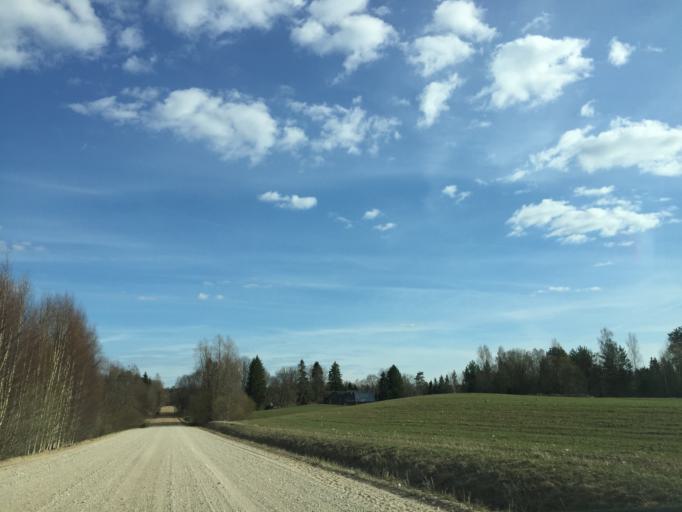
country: EE
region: Tartu
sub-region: Elva linn
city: Elva
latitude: 58.1189
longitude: 26.5304
